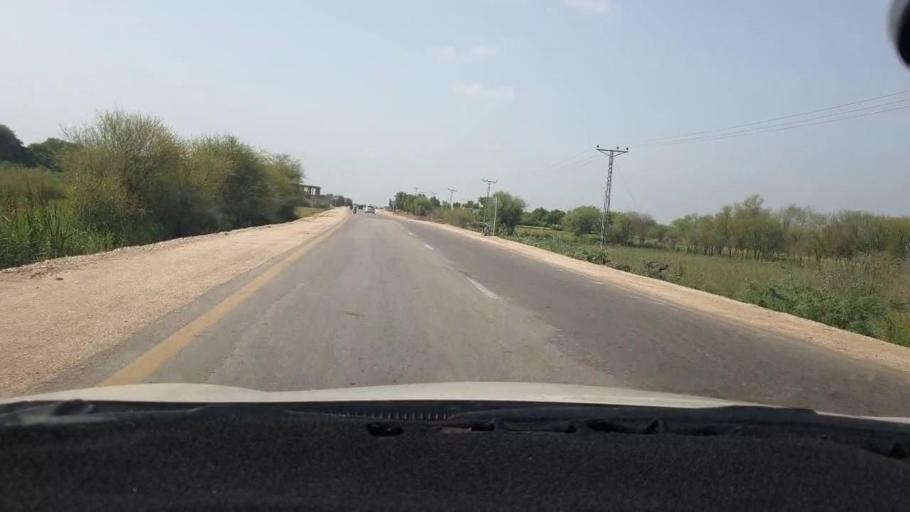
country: PK
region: Sindh
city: Mirpur Khas
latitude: 25.6994
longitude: 69.1226
